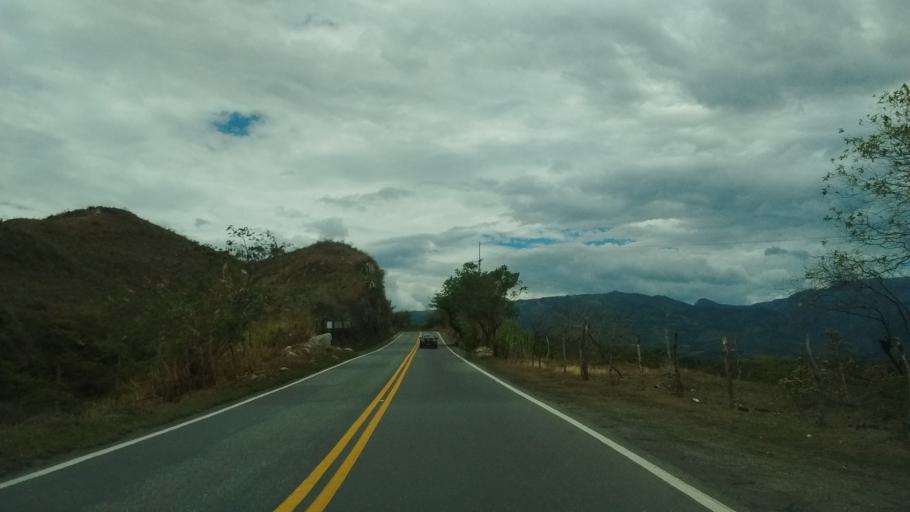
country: CO
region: Cauca
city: La Sierra
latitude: 2.2217
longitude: -76.7974
